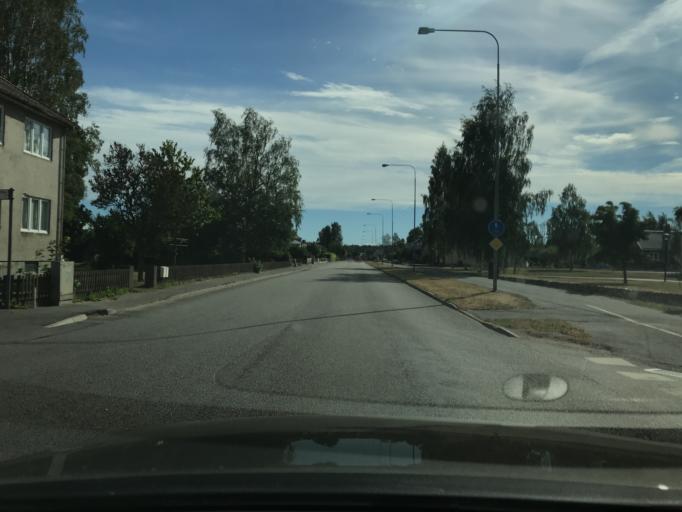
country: SE
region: Kalmar
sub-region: Hultsfreds Kommun
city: Hultsfred
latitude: 57.4948
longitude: 15.8469
